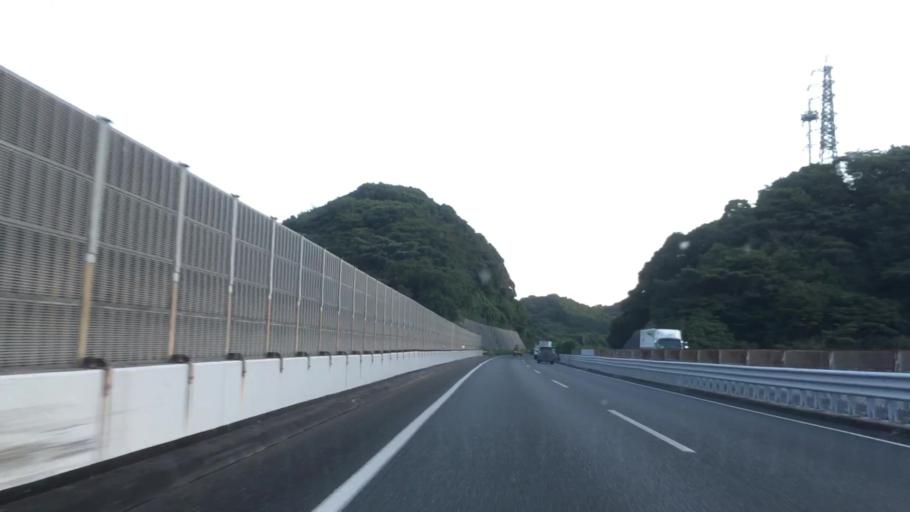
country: JP
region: Yamaguchi
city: Shimonoseki
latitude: 33.8989
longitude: 130.9719
